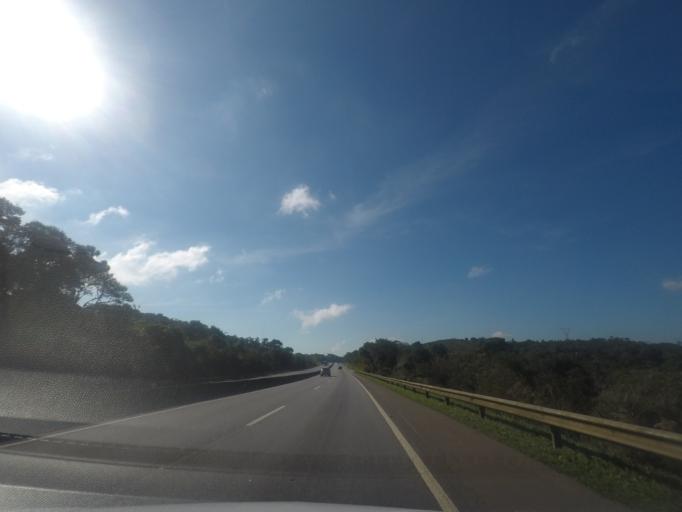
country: BR
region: Parana
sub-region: Piraquara
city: Piraquara
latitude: -25.5884
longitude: -48.9452
